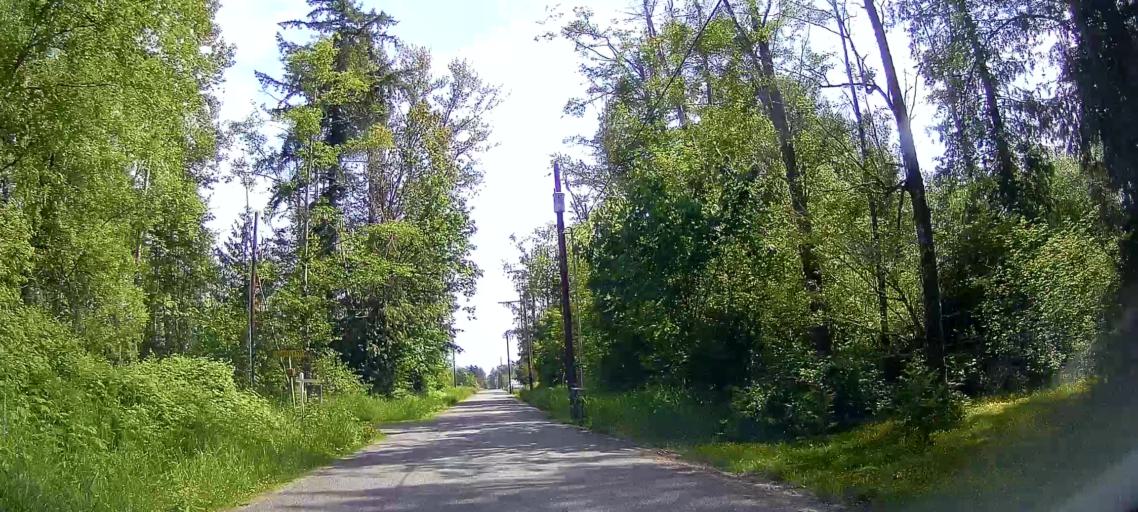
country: US
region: Washington
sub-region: Skagit County
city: Burlington
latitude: 48.5501
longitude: -122.3620
